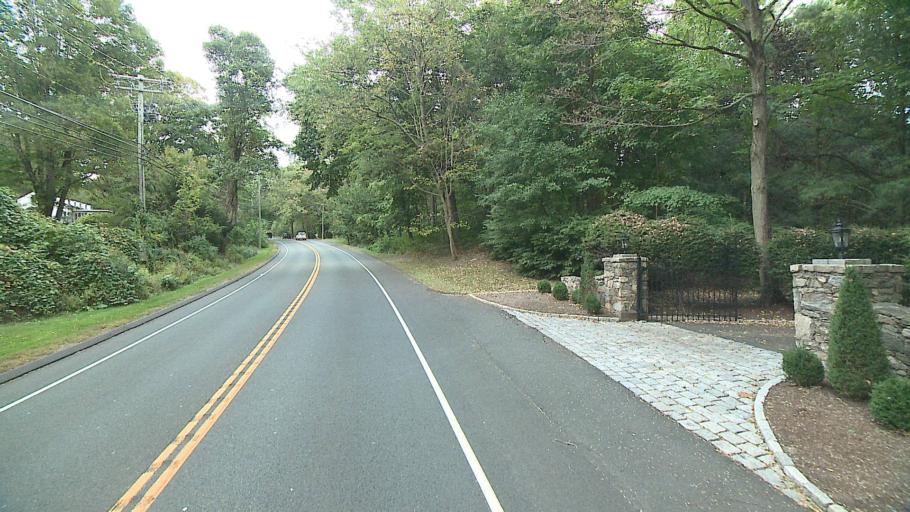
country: US
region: Connecticut
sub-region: Fairfield County
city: Westport
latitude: 41.1723
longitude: -73.3879
